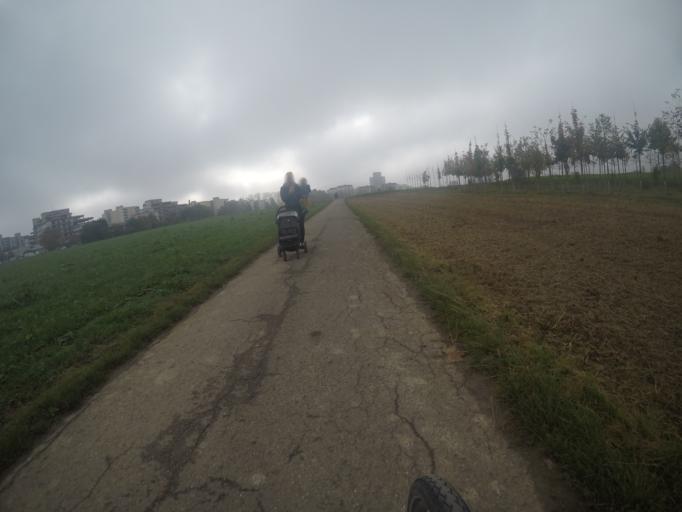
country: DE
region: Baden-Wuerttemberg
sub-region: Regierungsbezirk Stuttgart
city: Leinfelden-Echterdingen
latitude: 48.7341
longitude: 9.1337
